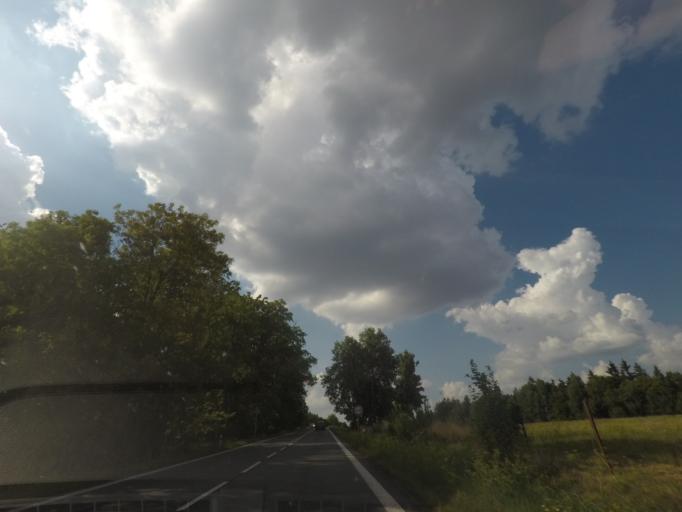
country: CZ
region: Kralovehradecky
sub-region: Okres Trutnov
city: Trutnov
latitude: 50.5301
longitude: 15.9152
